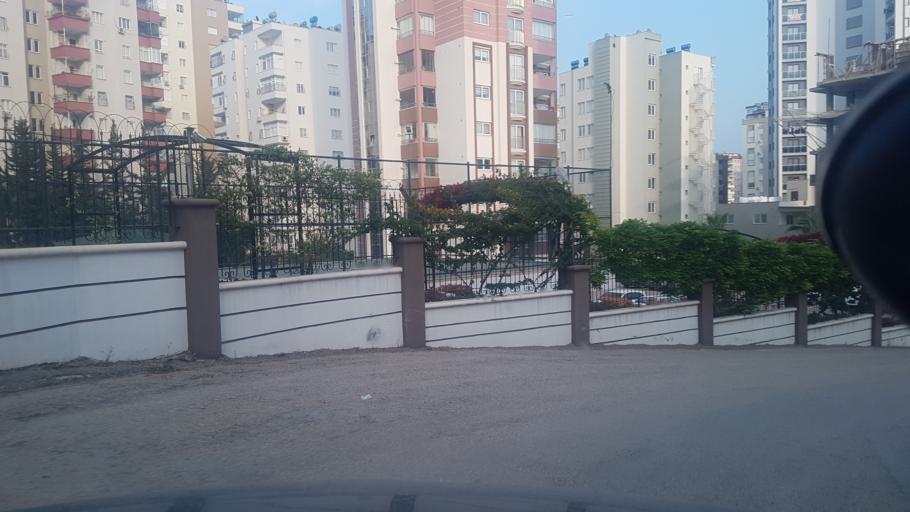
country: TR
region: Adana
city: Seyhan
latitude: 37.0467
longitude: 35.2760
